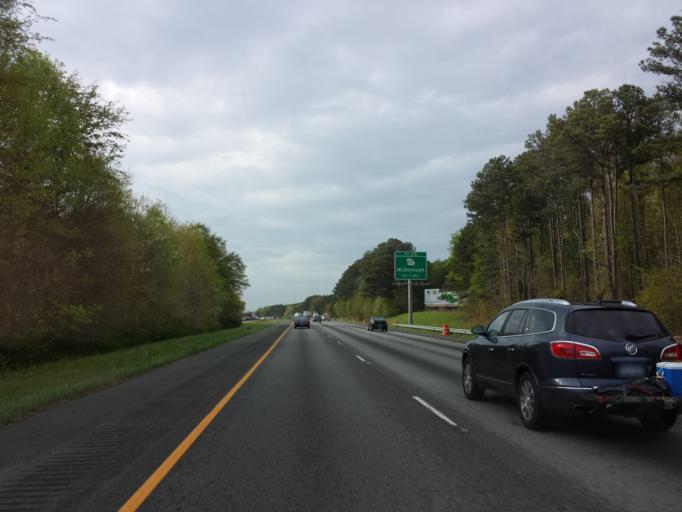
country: US
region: Georgia
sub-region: Henry County
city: McDonough
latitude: 33.4009
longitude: -84.1513
